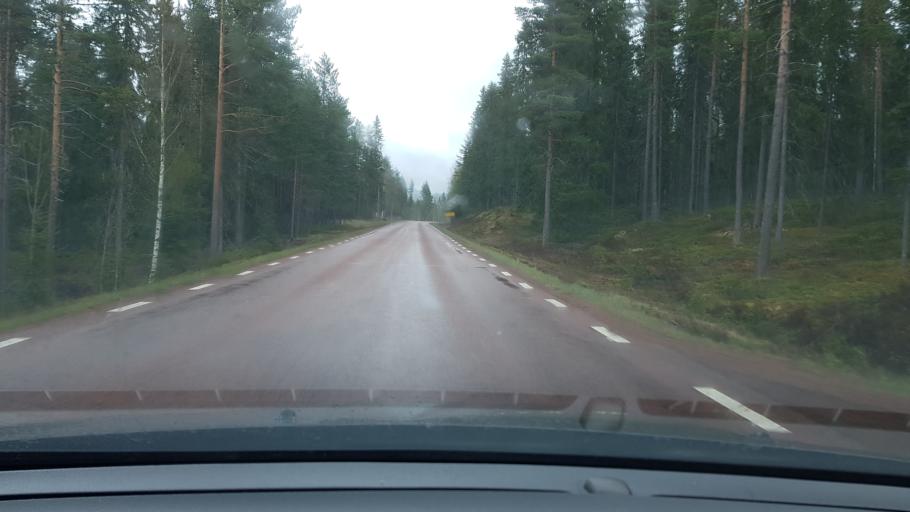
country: SE
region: Dalarna
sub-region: Alvdalens Kommun
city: AElvdalen
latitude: 61.1190
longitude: 14.0895
